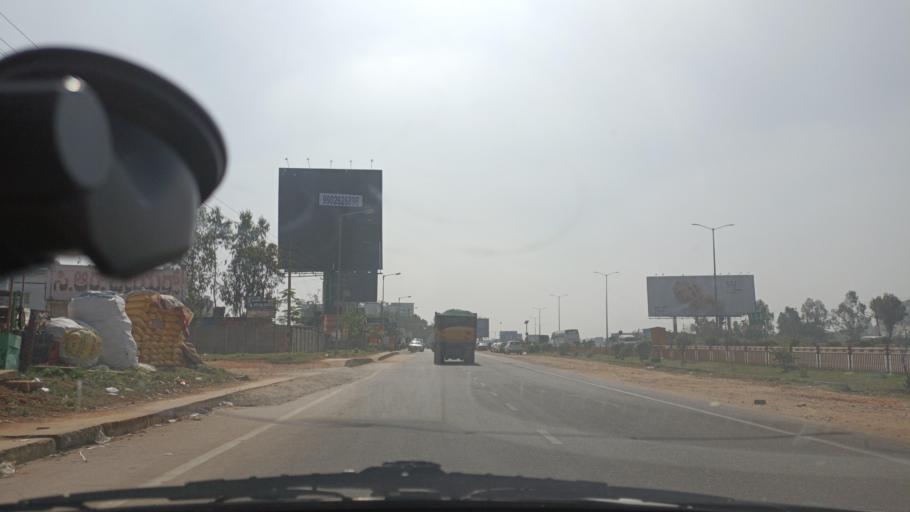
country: IN
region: Karnataka
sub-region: Bangalore Urban
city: Yelahanka
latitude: 13.1670
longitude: 77.6311
